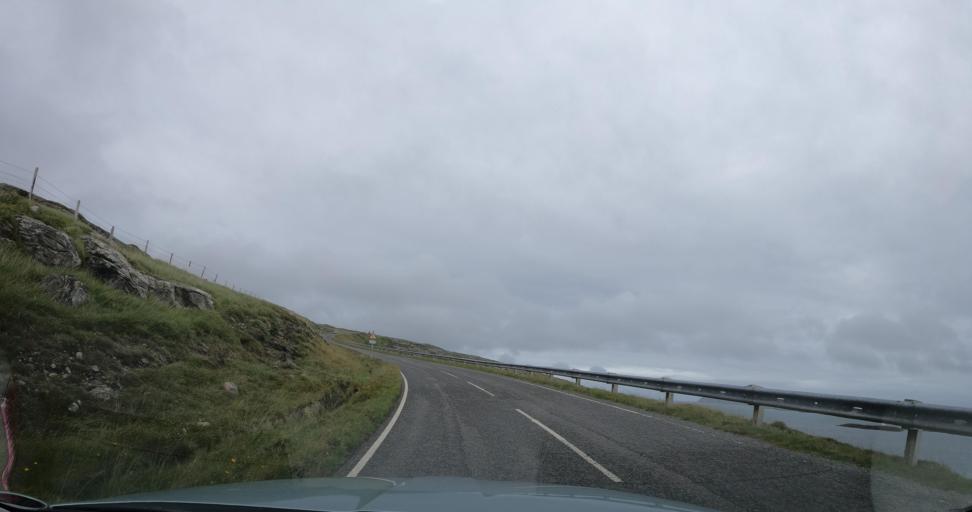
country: GB
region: Scotland
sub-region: Eilean Siar
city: Barra
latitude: 56.9480
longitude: -7.5181
